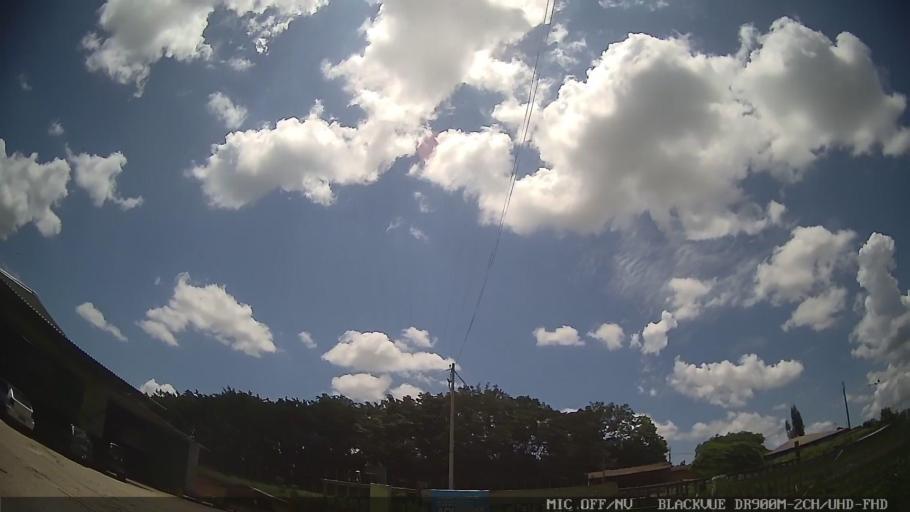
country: BR
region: Sao Paulo
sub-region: Itatiba
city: Itatiba
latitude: -22.8606
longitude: -46.7864
